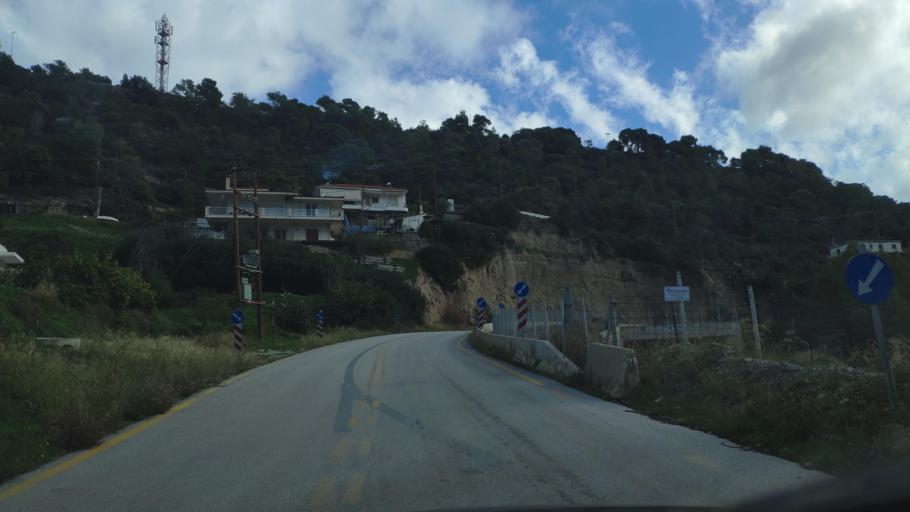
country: GR
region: West Greece
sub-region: Nomos Achaias
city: Aiyira
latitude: 38.1316
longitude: 22.4290
